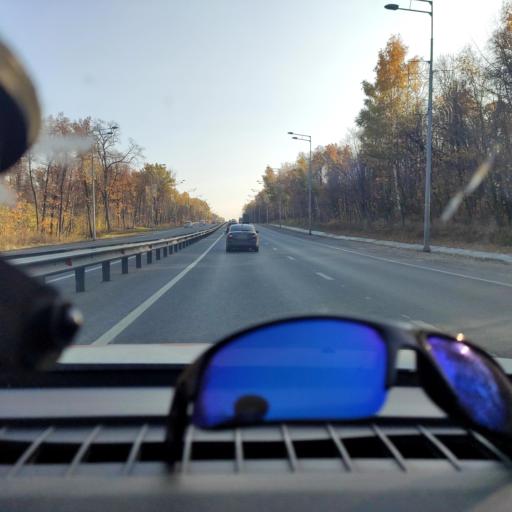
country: RU
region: Samara
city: Novosemeykino
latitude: 53.3330
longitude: 50.2318
